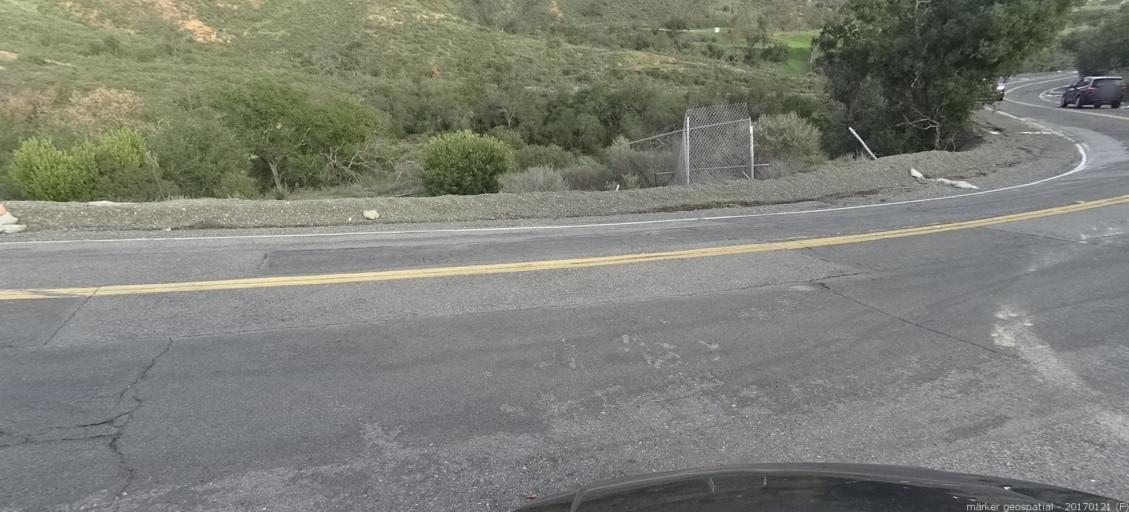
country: US
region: California
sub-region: Orange County
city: Portola Hills
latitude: 33.7003
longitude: -117.6359
